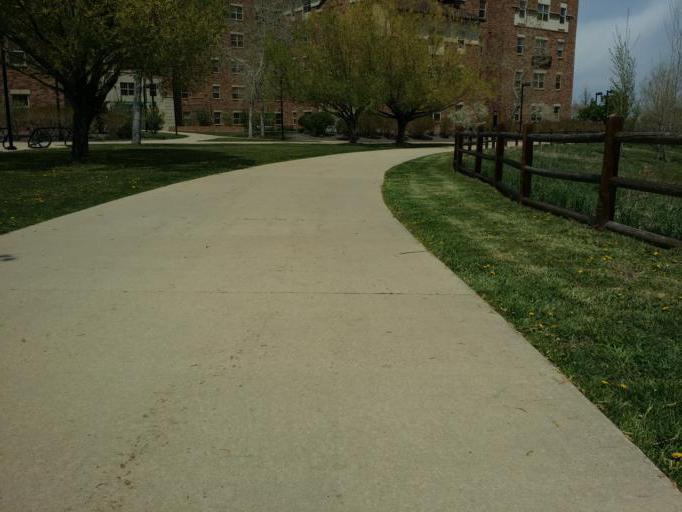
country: US
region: Colorado
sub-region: Boulder County
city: Boulder
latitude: 39.9960
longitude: -105.2490
